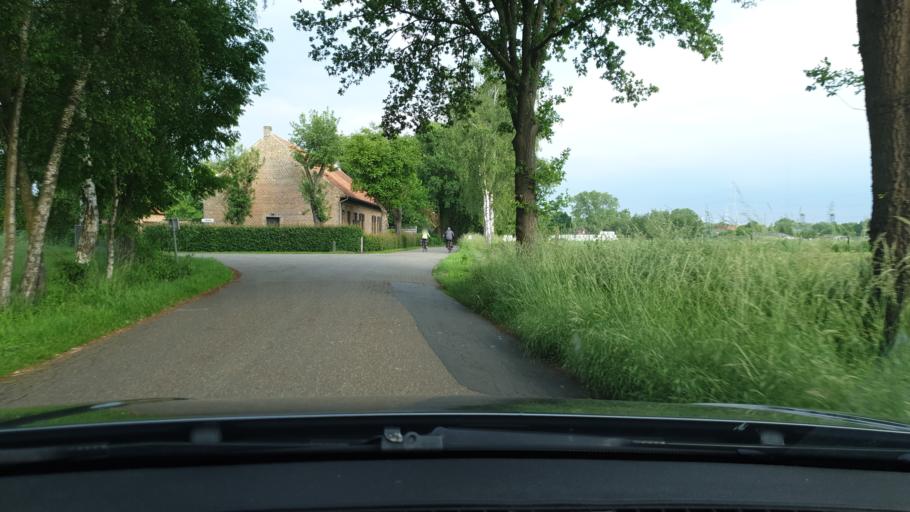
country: BE
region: Flanders
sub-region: Provincie Antwerpen
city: Geel
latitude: 51.1339
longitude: 4.9757
